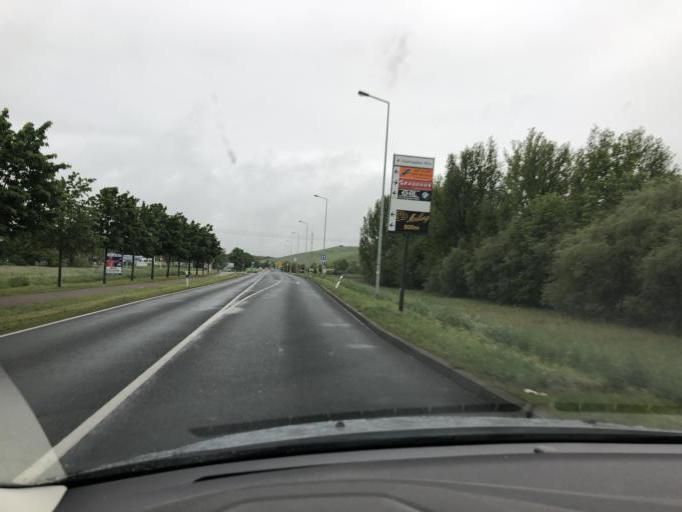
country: DE
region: Saxony-Anhalt
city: Dessau
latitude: 51.8149
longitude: 12.2156
